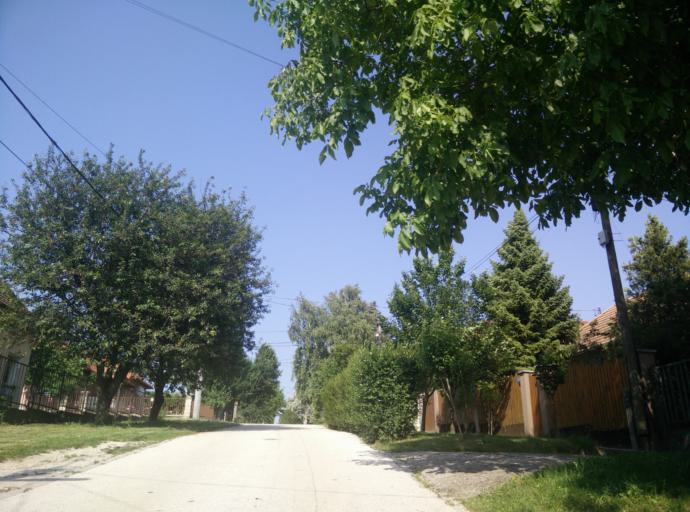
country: HU
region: Pest
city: Biatorbagy
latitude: 47.4695
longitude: 18.8065
